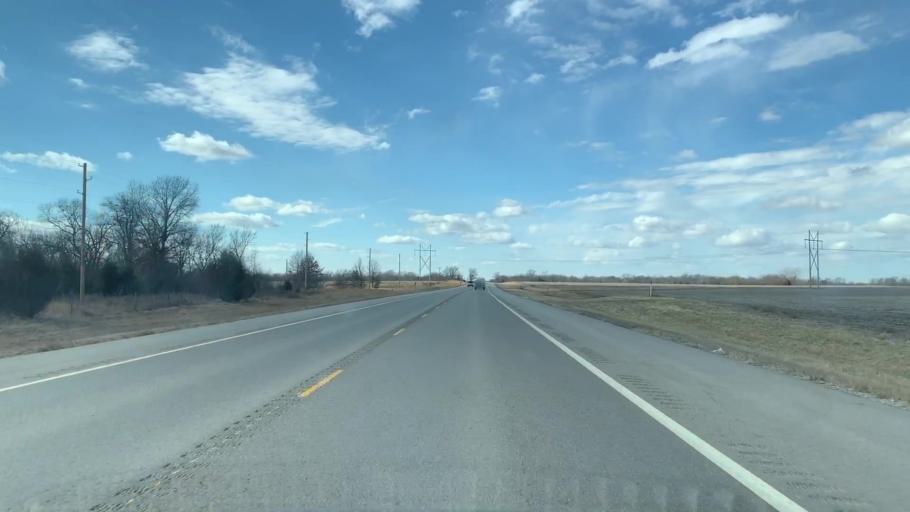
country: US
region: Kansas
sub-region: Labette County
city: Oswego
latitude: 37.3400
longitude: -95.0755
